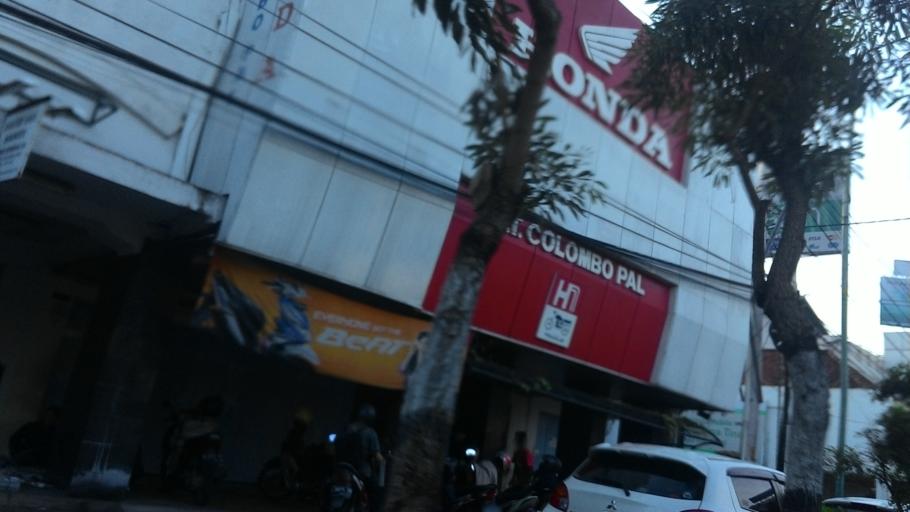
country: ID
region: Daerah Istimewa Yogyakarta
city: Yogyakarta
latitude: -7.7861
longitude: 110.3667
